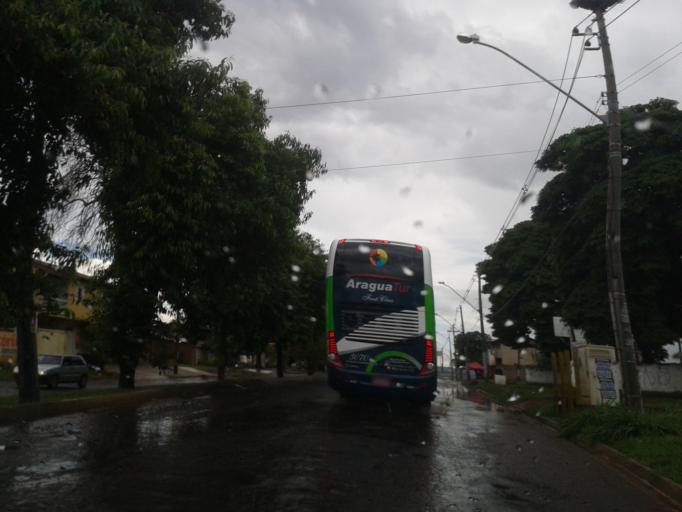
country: BR
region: Goias
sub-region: Goiania
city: Goiania
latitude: -16.6668
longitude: -49.3304
